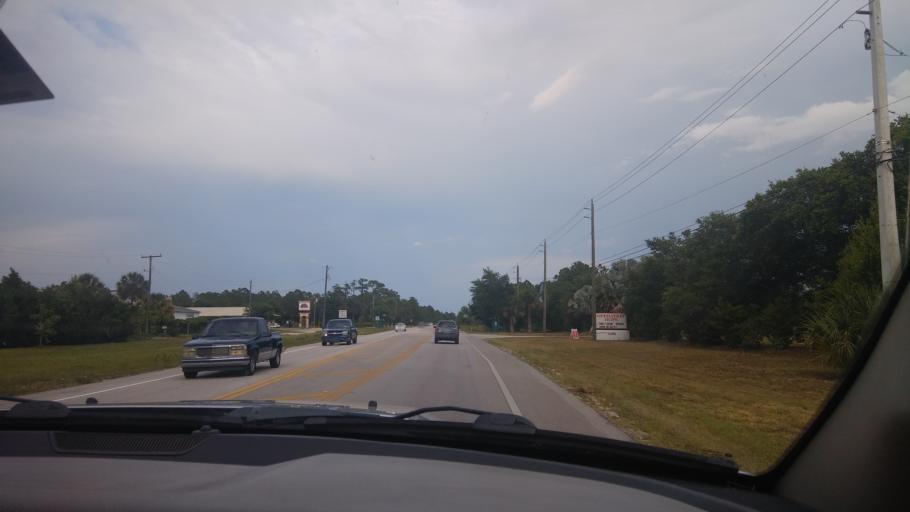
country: US
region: Florida
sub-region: Indian River County
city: Fellsmere
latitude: 27.7676
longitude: -80.5787
